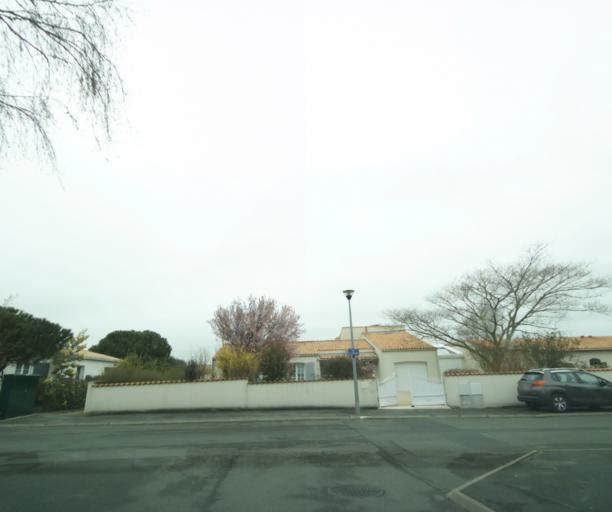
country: FR
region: Poitou-Charentes
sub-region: Departement de la Charente-Maritime
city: Lagord
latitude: 46.1859
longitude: -1.1426
